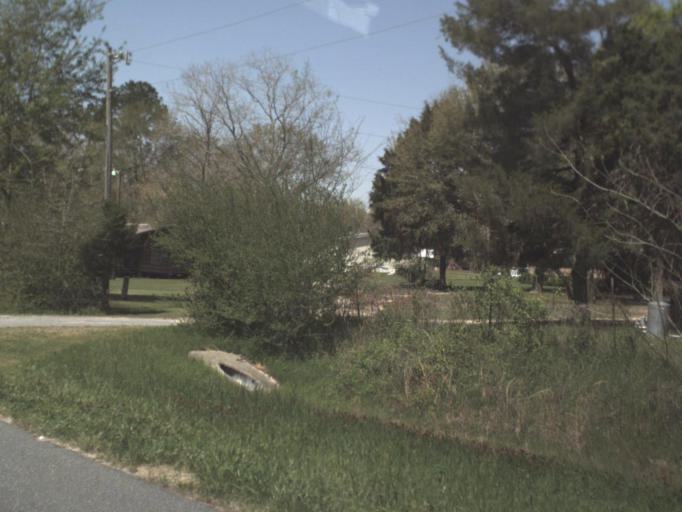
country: US
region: Florida
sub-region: Jackson County
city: Graceville
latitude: 30.9726
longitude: -85.6360
